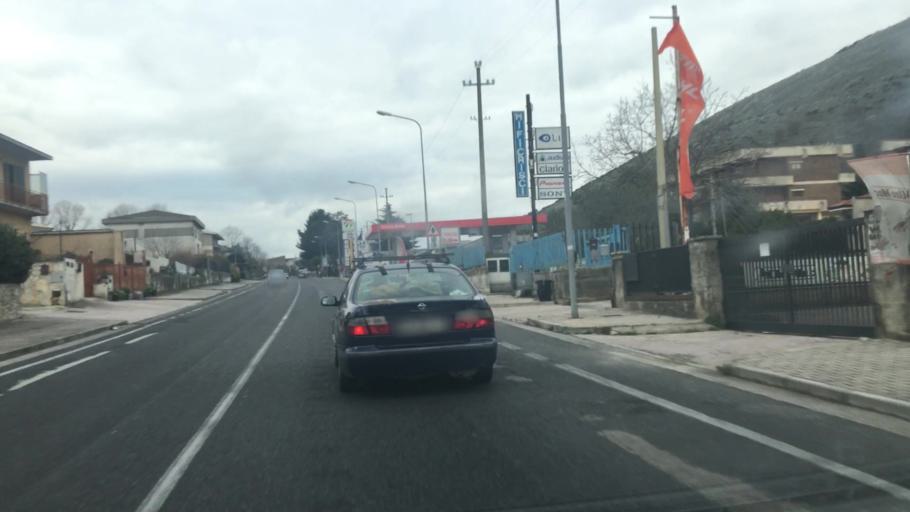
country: IT
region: Campania
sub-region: Provincia di Benevento
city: Arpaia
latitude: 41.0393
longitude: 14.5563
